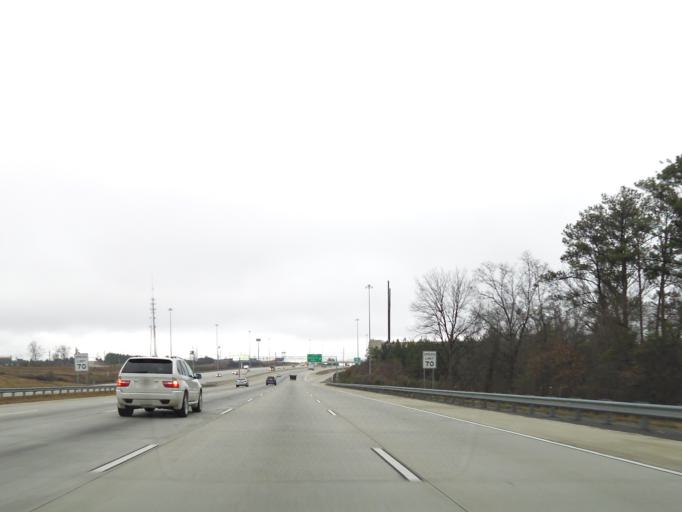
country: US
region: Georgia
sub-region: Peach County
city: Byron
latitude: 32.7367
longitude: -83.7225
